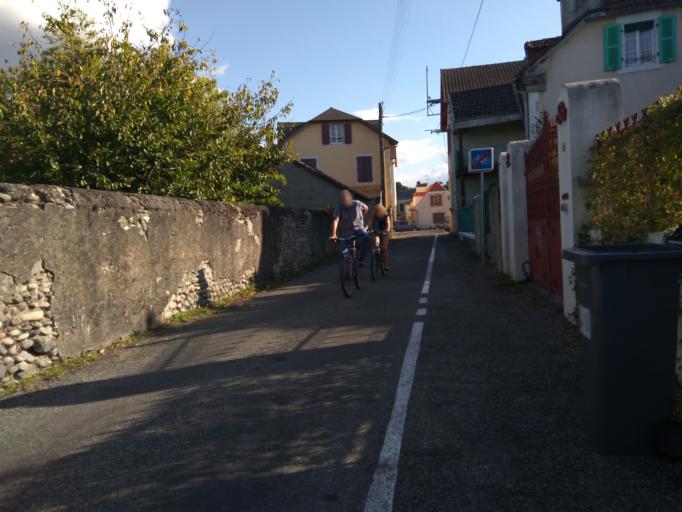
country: FR
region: Aquitaine
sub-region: Departement des Pyrenees-Atlantiques
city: Gelos
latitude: 43.2837
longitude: -0.3718
